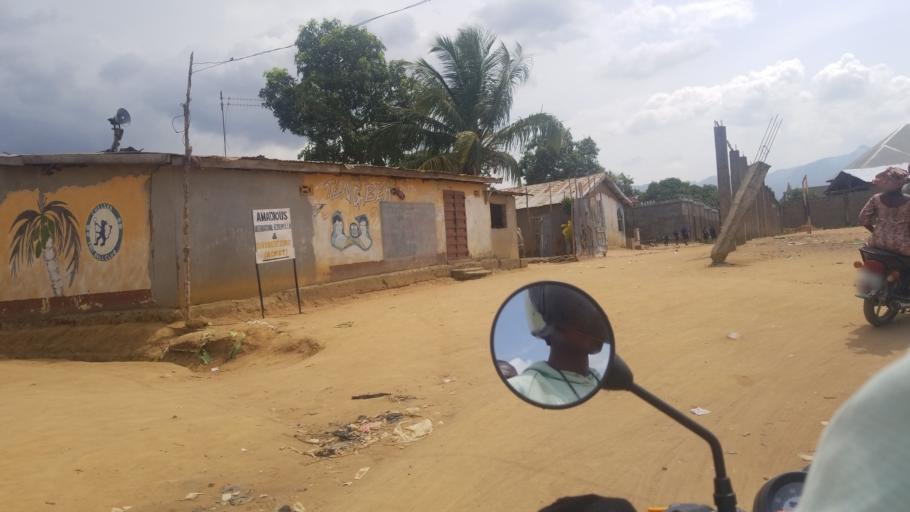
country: SL
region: Western Area
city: Waterloo
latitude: 8.3269
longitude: -13.0485
